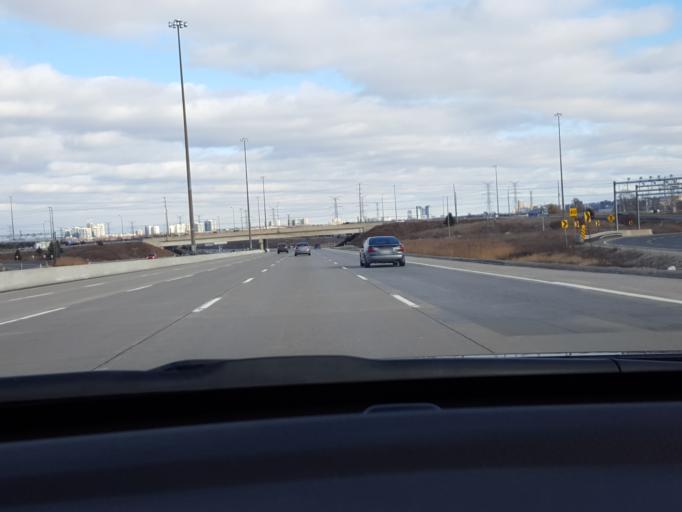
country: CA
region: Ontario
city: Concord
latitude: 43.7913
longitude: -79.5015
